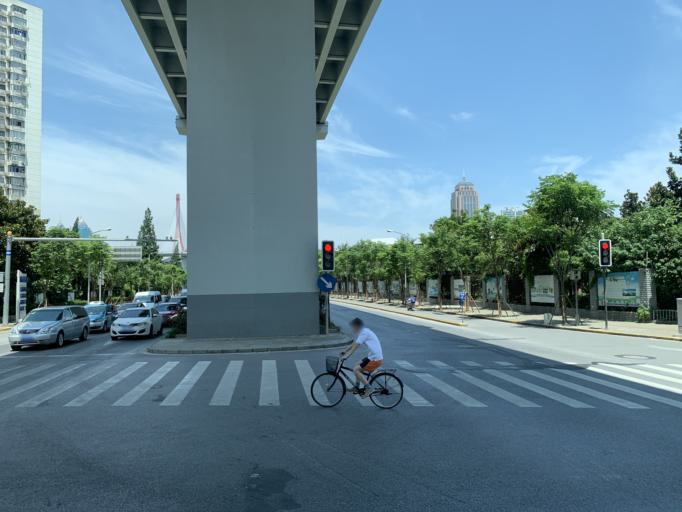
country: CN
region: Shanghai Shi
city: Pudong
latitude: 31.2486
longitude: 121.5541
